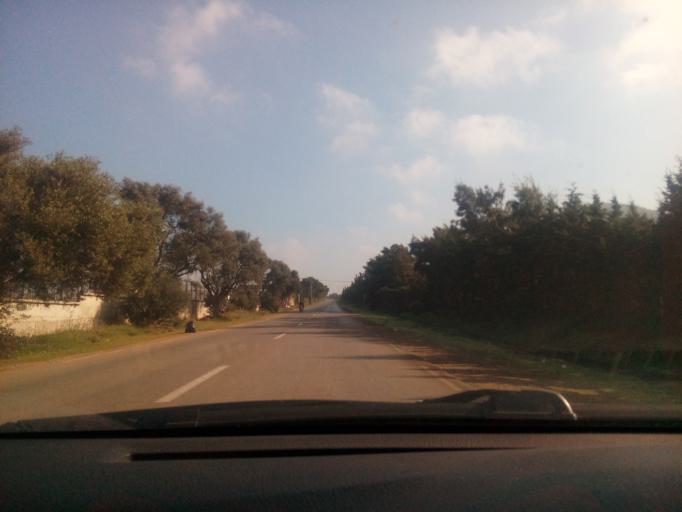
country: DZ
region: Oran
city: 'Ain el Turk
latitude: 35.7035
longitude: -0.8454
